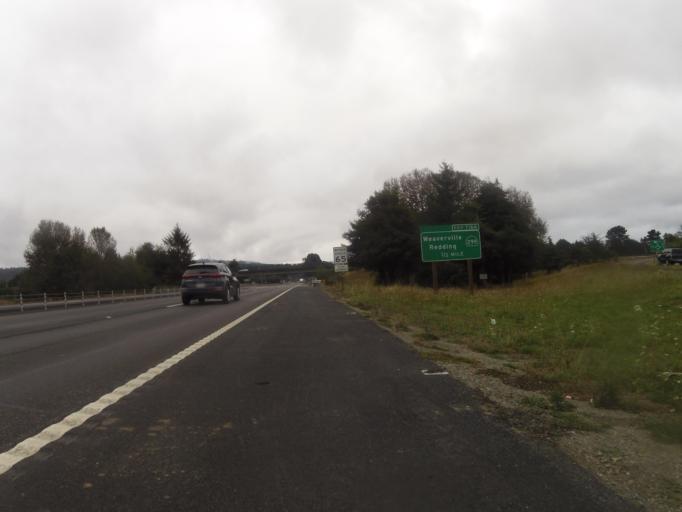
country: US
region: California
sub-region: Humboldt County
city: Arcata
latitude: 40.9067
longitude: -124.0884
